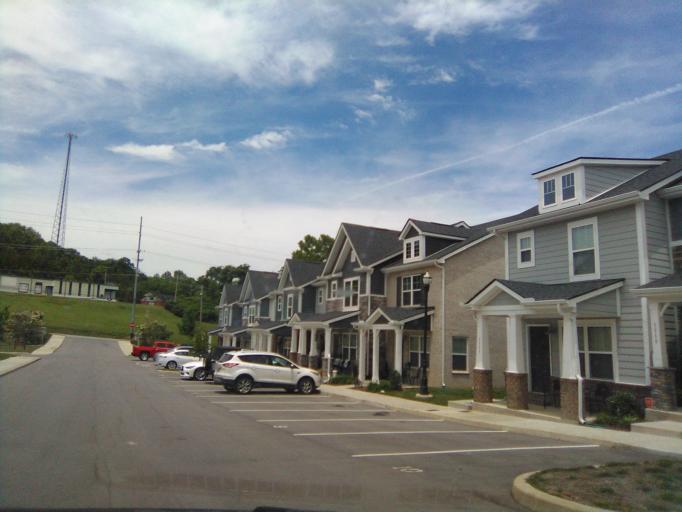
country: US
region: Tennessee
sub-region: Davidson County
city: Belle Meade
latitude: 36.1258
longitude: -86.9079
